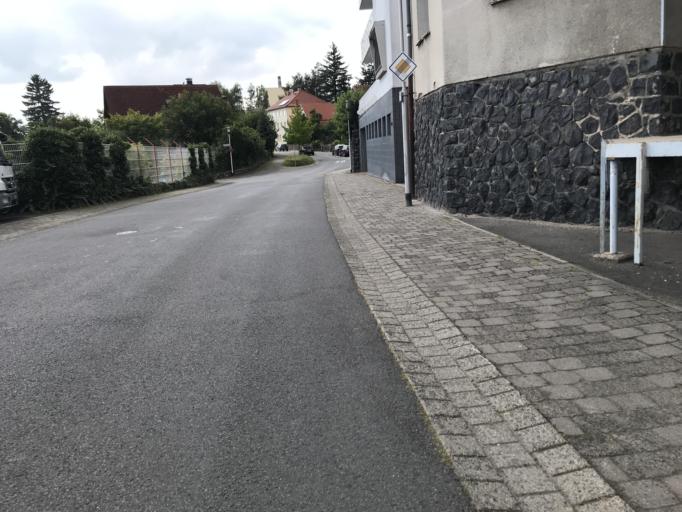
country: DE
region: Hesse
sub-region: Regierungsbezirk Giessen
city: Lauterbach
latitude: 50.6402
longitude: 9.3965
